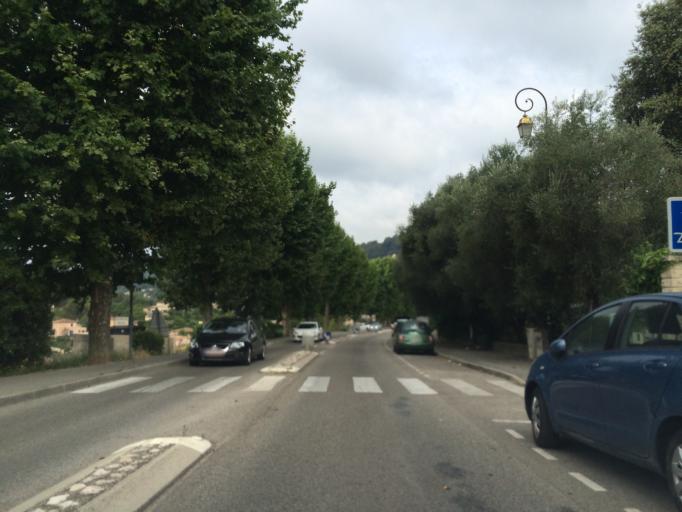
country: FR
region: Provence-Alpes-Cote d'Azur
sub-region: Departement des Alpes-Maritimes
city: La Colle-sur-Loup
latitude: 43.6850
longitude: 7.1074
